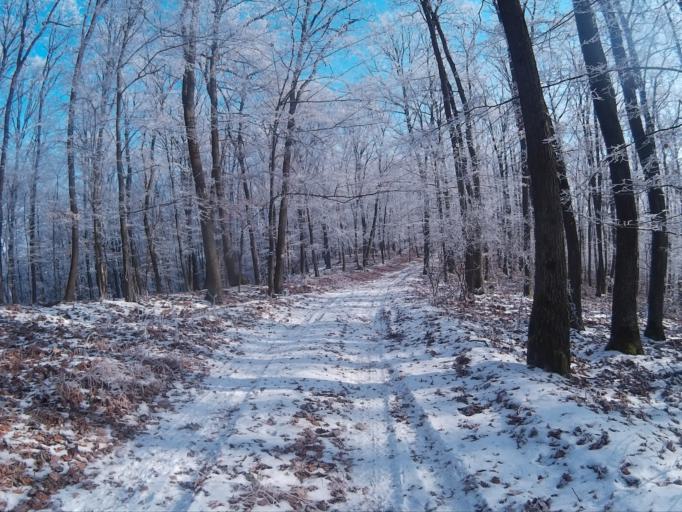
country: HU
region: Borsod-Abauj-Zemplen
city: Szendro
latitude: 48.5016
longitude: 20.7535
